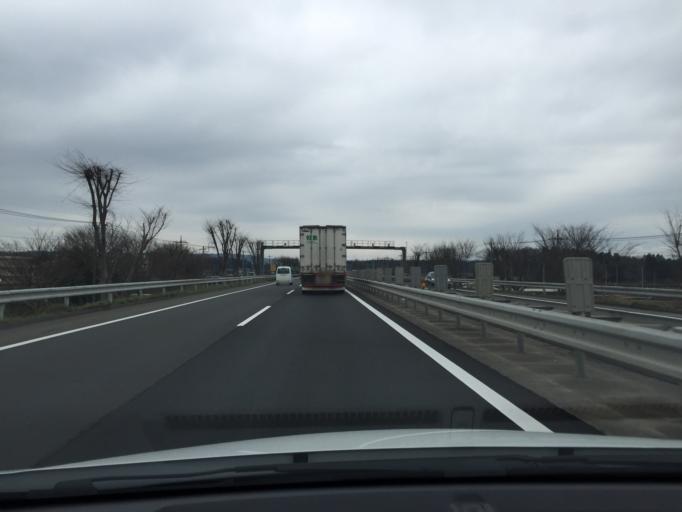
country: JP
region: Saitama
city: Sayama
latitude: 35.8579
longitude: 139.3731
